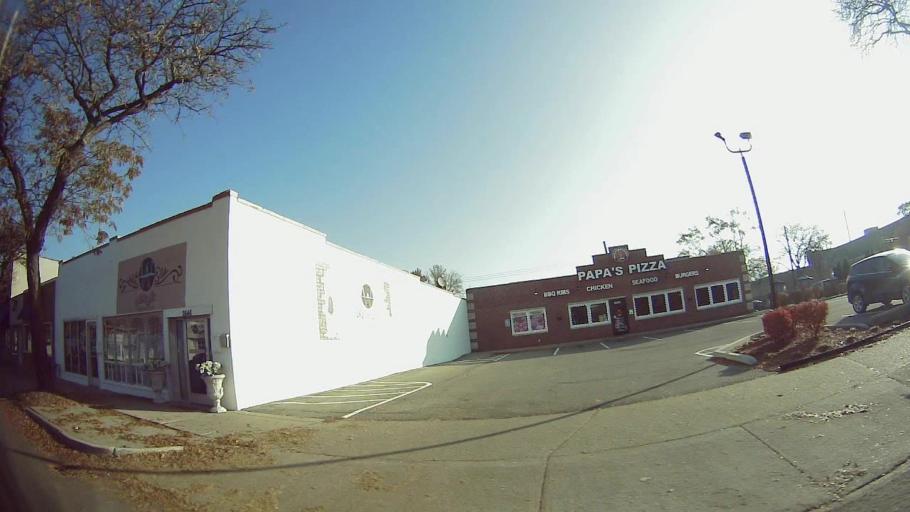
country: US
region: Michigan
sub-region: Oakland County
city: Berkley
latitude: 42.4963
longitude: -83.1836
